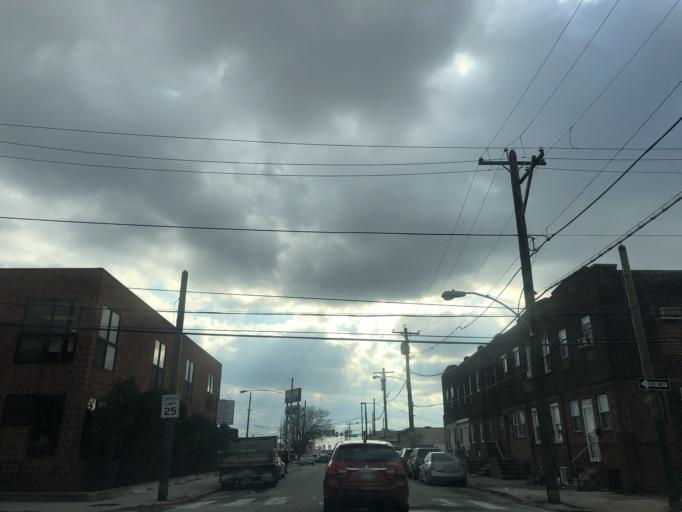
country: US
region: Pennsylvania
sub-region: Philadelphia County
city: Philadelphia
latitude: 39.9239
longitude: -75.1849
